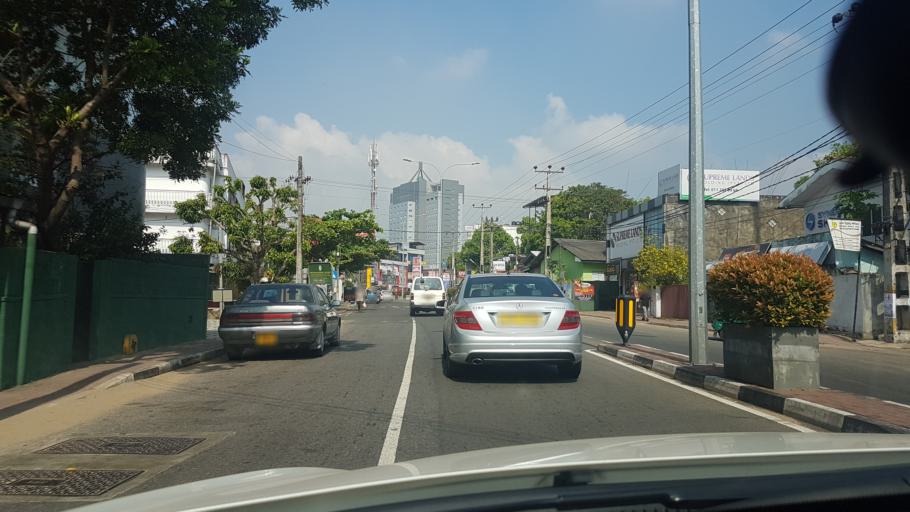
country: LK
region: Western
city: Battaramulla South
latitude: 6.9002
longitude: 79.9213
